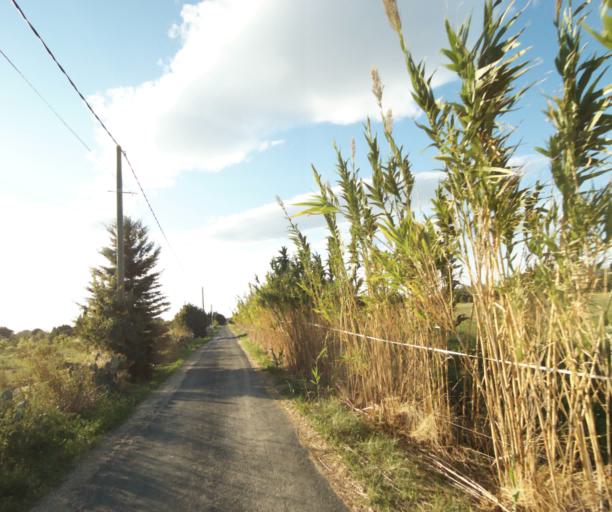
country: FR
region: Languedoc-Roussillon
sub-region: Departement des Pyrenees-Orientales
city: Latour-Bas-Elne
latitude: 42.5805
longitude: 2.9996
